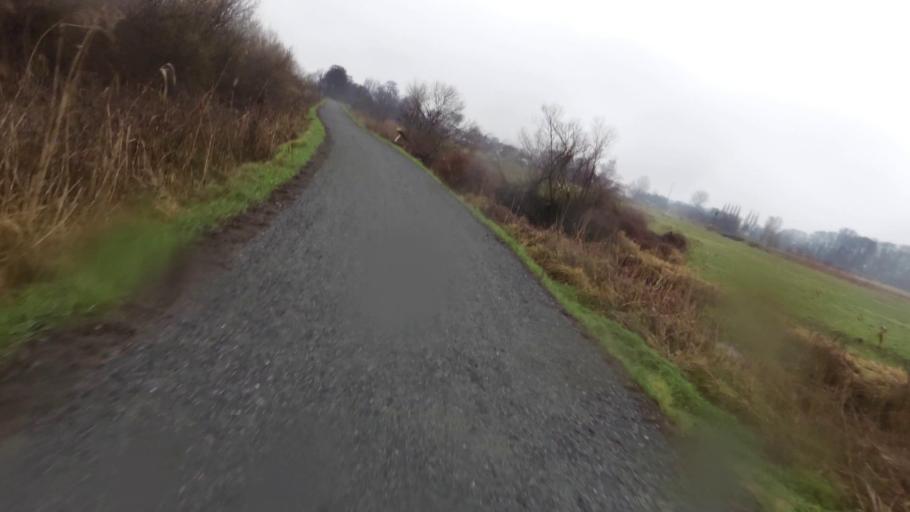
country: PL
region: West Pomeranian Voivodeship
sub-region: Powiat policki
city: Police
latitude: 53.4994
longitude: 14.7011
